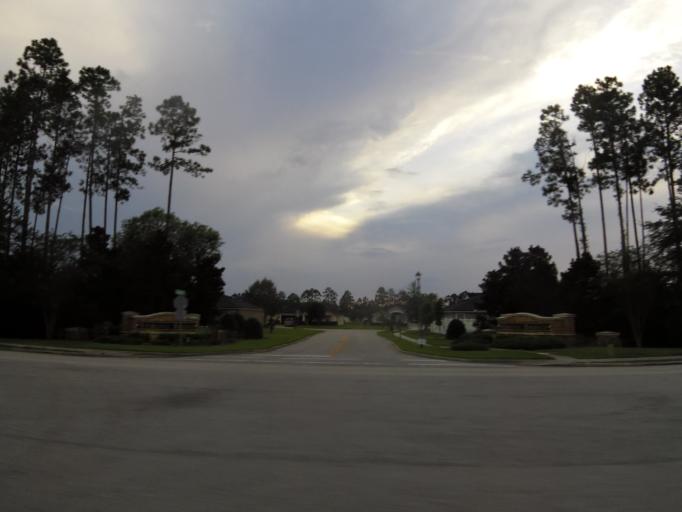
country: US
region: Florida
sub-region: Saint Johns County
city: Fruit Cove
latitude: 30.0781
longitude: -81.6018
